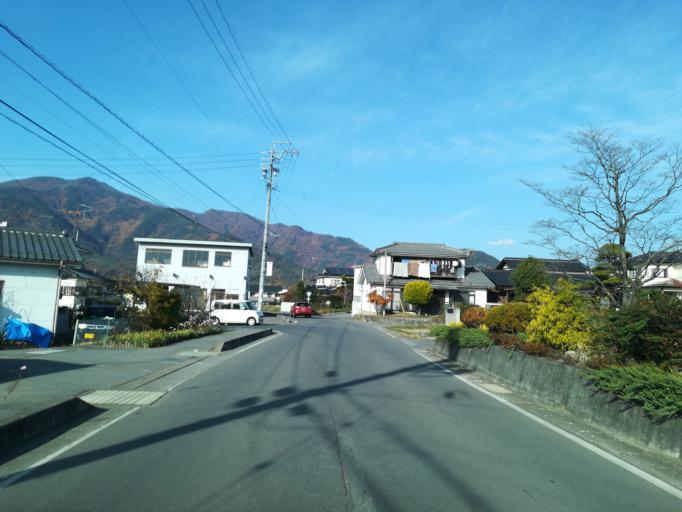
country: JP
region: Nagano
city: Ueda
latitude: 36.4045
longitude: 138.2802
